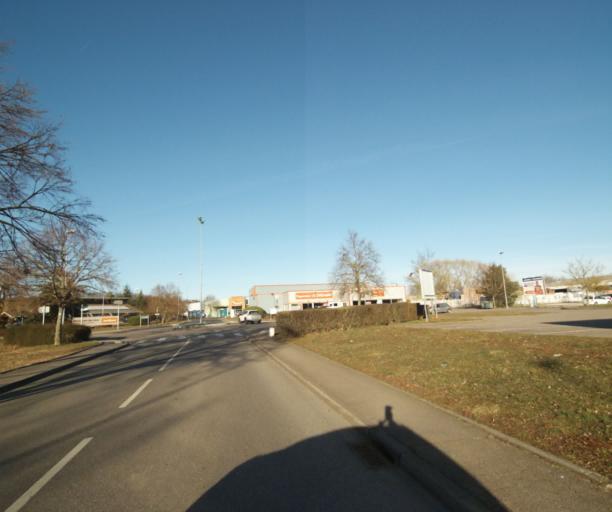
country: FR
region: Lorraine
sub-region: Departement de Meurthe-et-Moselle
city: Pulnoy
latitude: 48.7089
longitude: 6.2491
